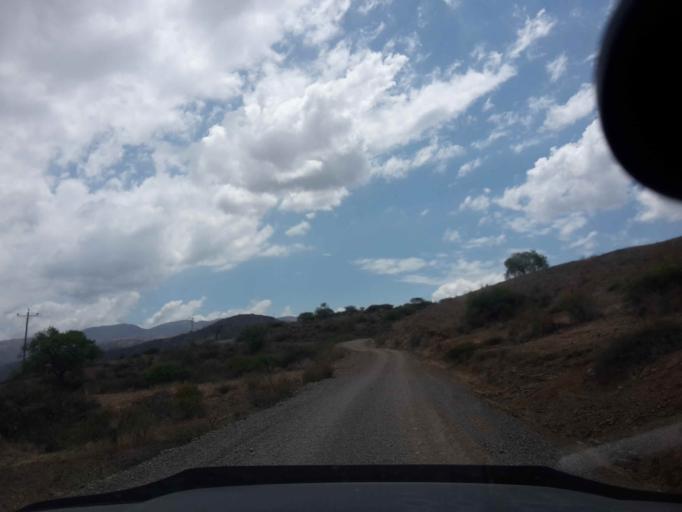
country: BO
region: Cochabamba
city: Sipe Sipe
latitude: -17.5418
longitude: -66.4830
